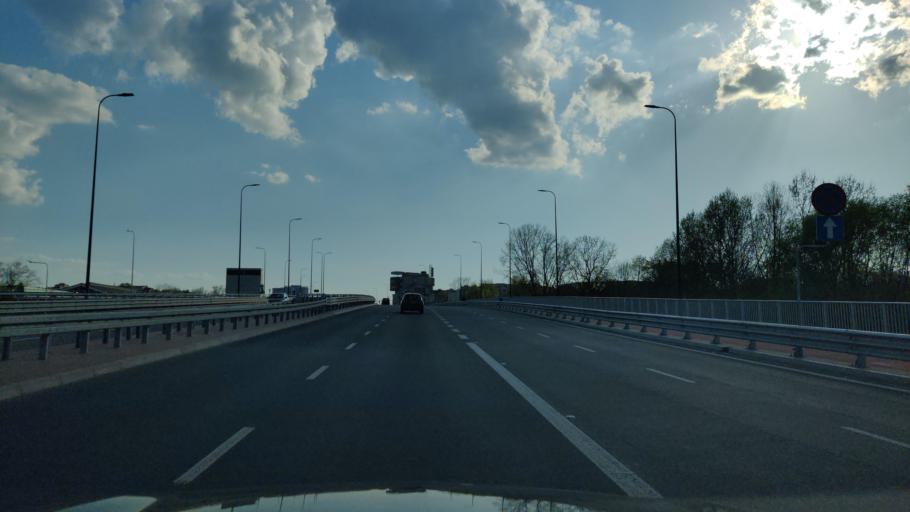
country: PL
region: Masovian Voivodeship
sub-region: Warszawa
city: Ursynow
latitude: 52.1523
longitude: 21.0655
